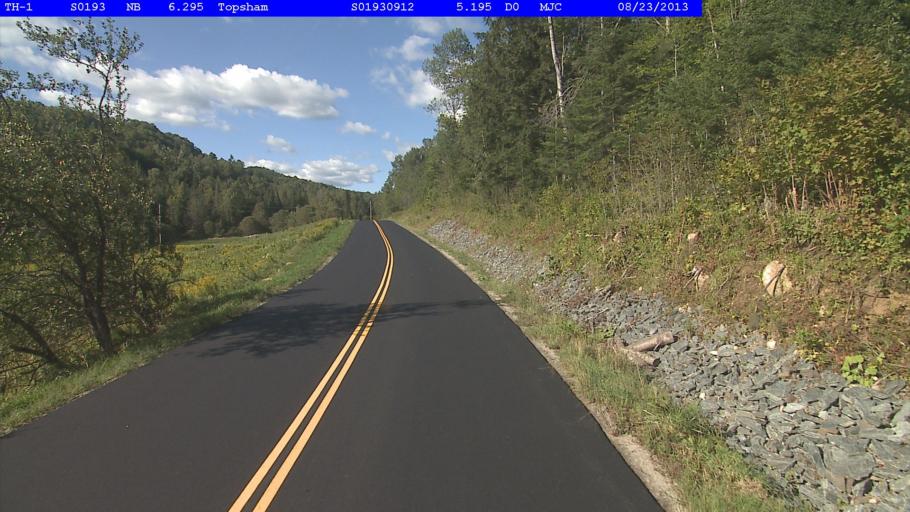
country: US
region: New Hampshire
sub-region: Grafton County
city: Woodsville
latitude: 44.1375
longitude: -72.2392
